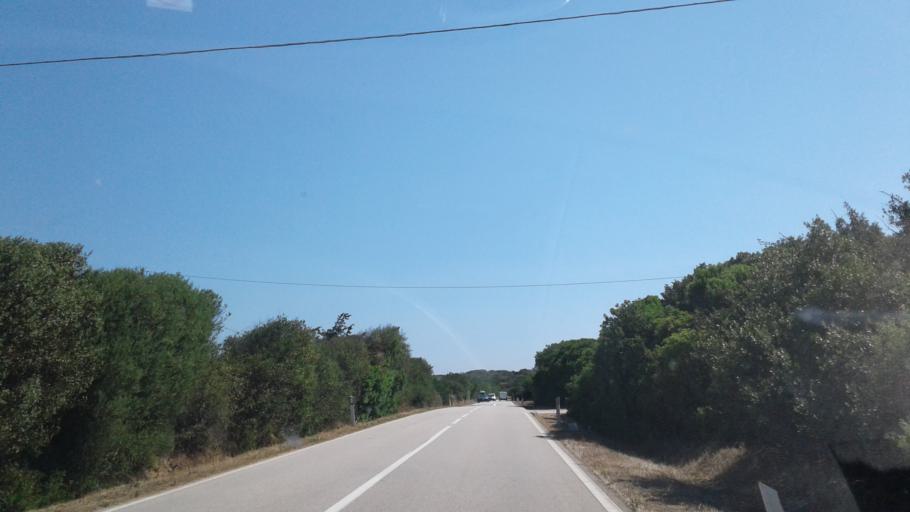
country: IT
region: Sardinia
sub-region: Provincia di Olbia-Tempio
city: Luogosanto
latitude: 41.1244
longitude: 9.2749
